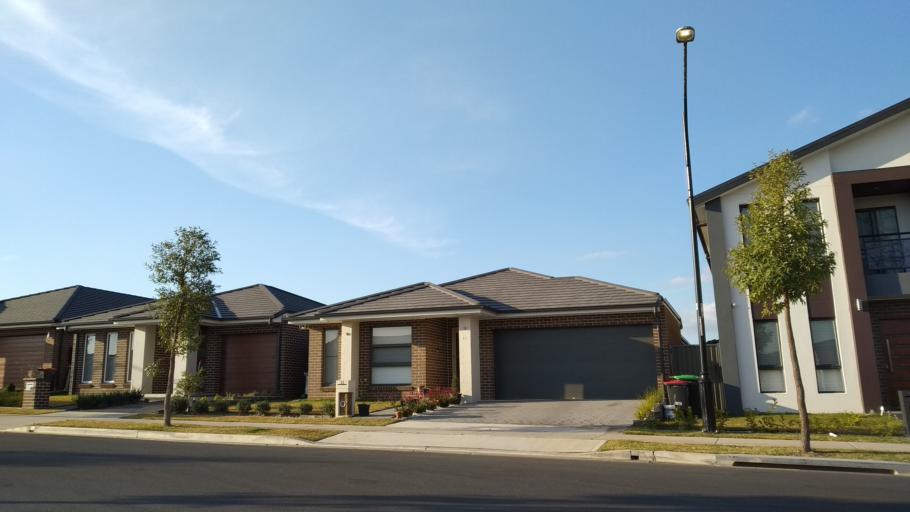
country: AU
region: New South Wales
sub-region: Penrith Municipality
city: Werrington County
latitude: -33.7381
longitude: 150.7521
